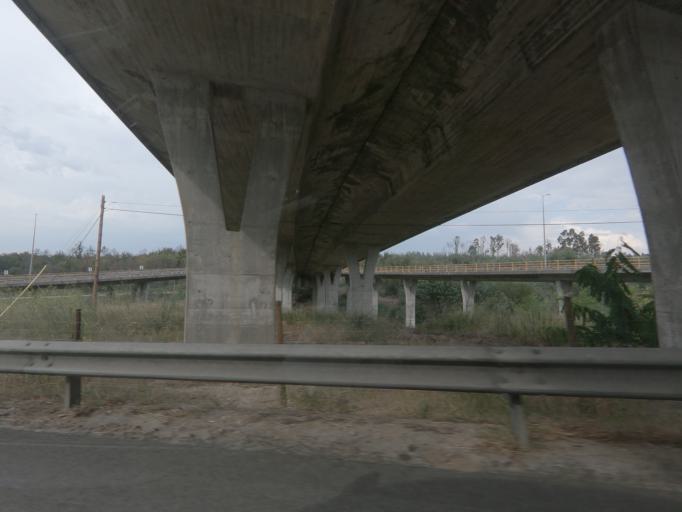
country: PT
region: Viseu
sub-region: Santa Comba Dao
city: Santa Comba Dao
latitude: 40.3832
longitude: -8.1178
